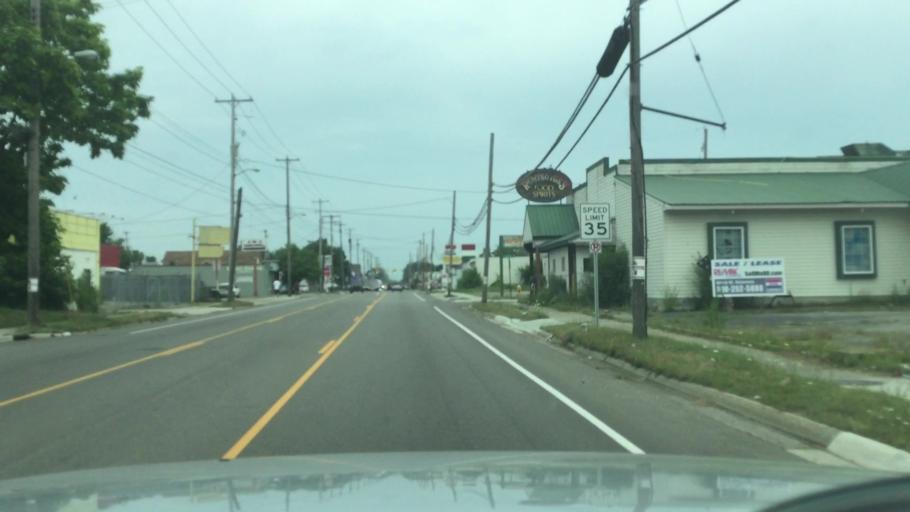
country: US
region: Michigan
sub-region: Genesee County
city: Flint
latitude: 42.9859
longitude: -83.6930
